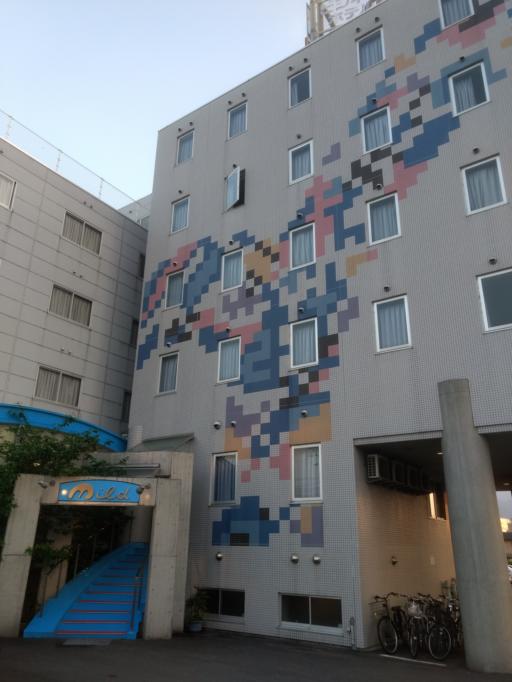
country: JP
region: Ehime
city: Kawanoecho
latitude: 33.9846
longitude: 133.5538
